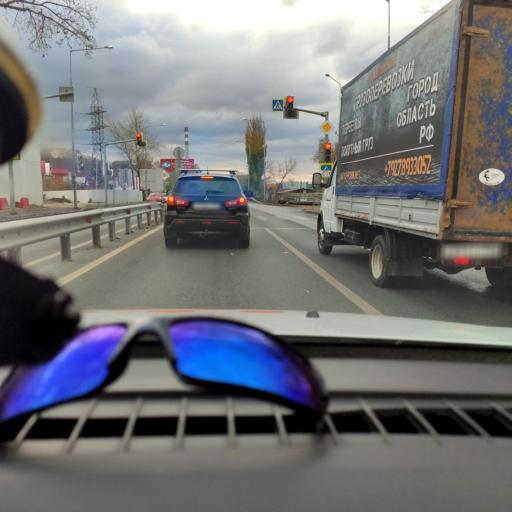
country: RU
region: Samara
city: Volzhskiy
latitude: 53.3855
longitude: 50.1633
